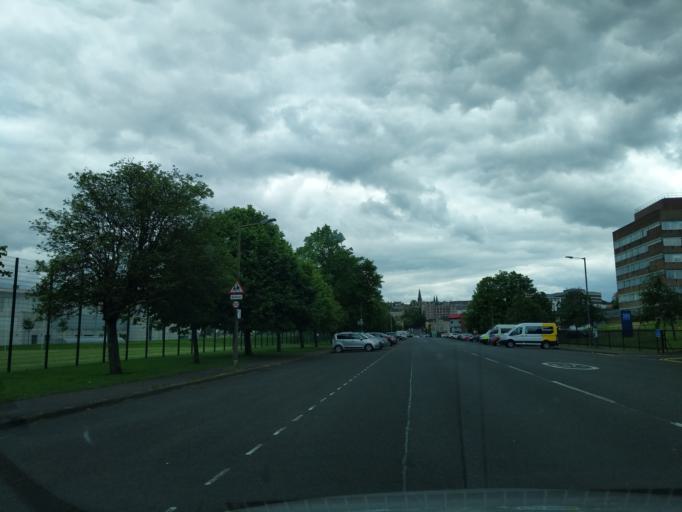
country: GB
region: Scotland
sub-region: Edinburgh
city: Edinburgh
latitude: 55.9615
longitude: -3.2245
